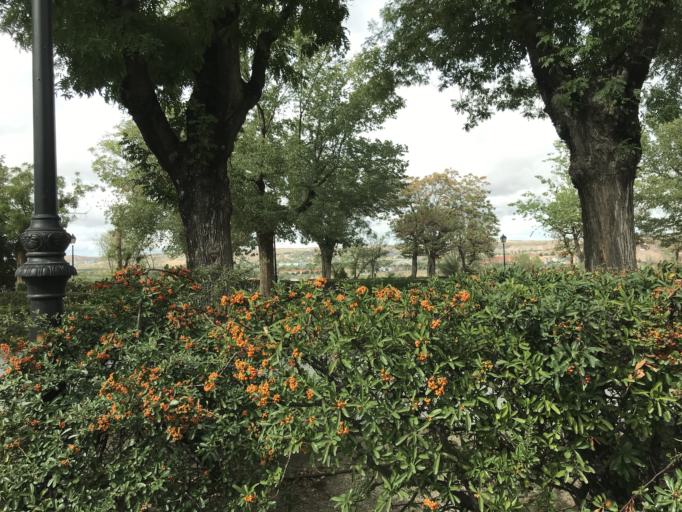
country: ES
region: Castille-La Mancha
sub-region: Province of Toledo
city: Toledo
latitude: 39.8597
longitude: -4.0320
